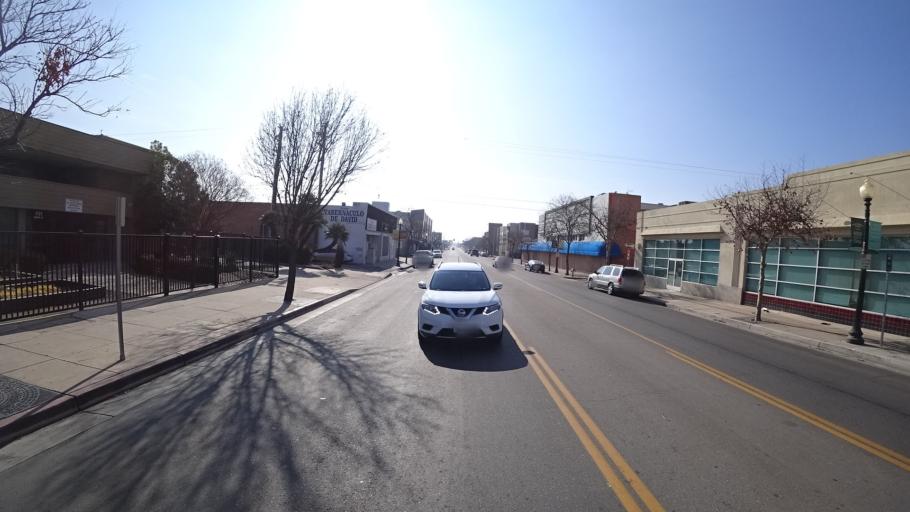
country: US
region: California
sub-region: Kern County
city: Bakersfield
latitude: 35.3807
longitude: -118.9915
